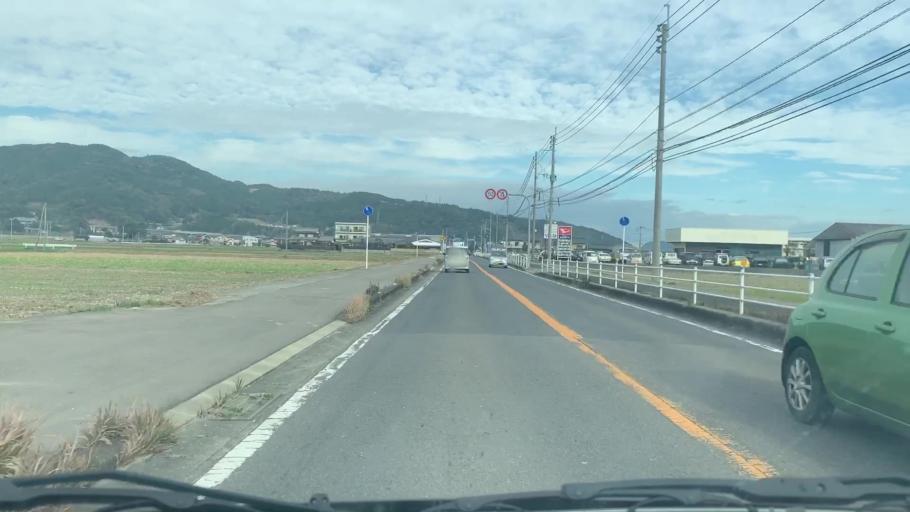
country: JP
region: Saga Prefecture
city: Karatsu
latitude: 33.4018
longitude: 129.9869
